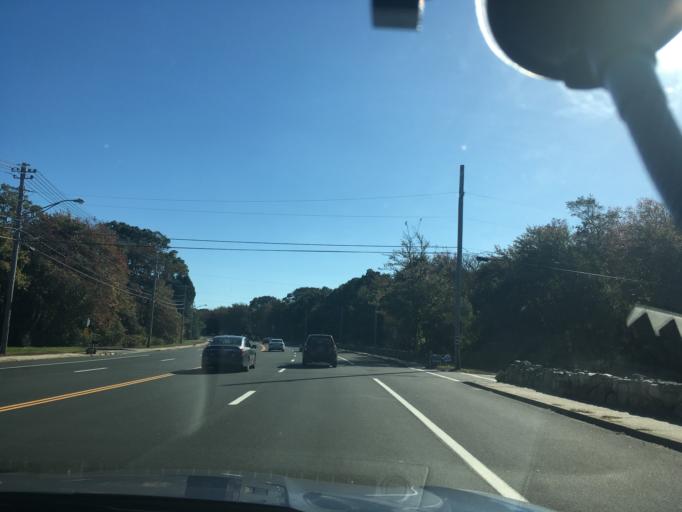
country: US
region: Rhode Island
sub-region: Washington County
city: Narragansett Pier
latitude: 41.4222
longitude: -71.4815
